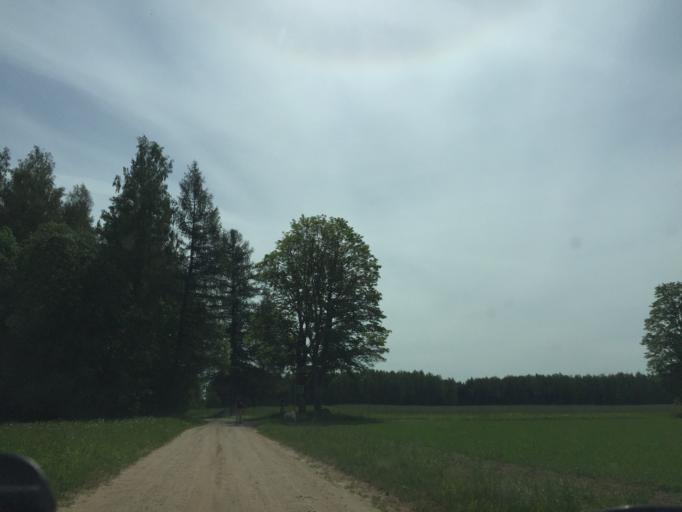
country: LV
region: Koceni
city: Koceni
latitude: 57.4455
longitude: 25.2807
